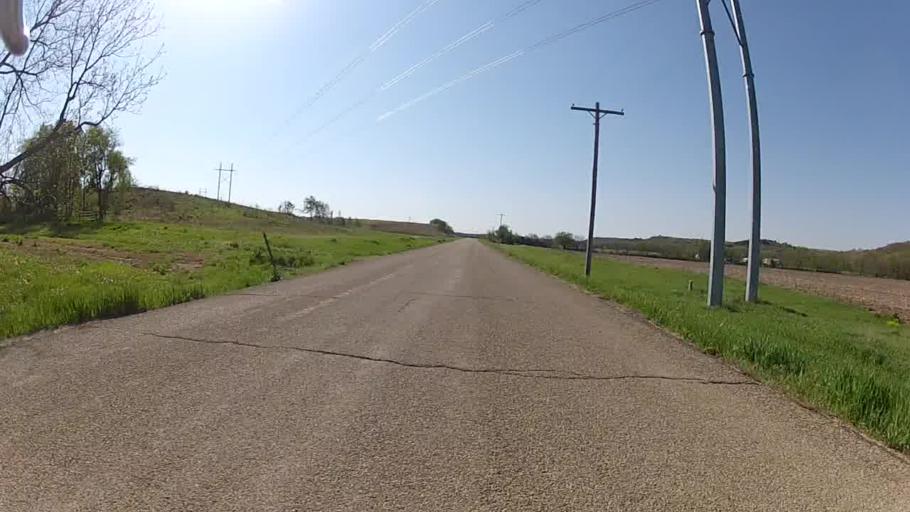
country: US
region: Kansas
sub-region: Riley County
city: Ogden
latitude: 39.0218
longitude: -96.6935
